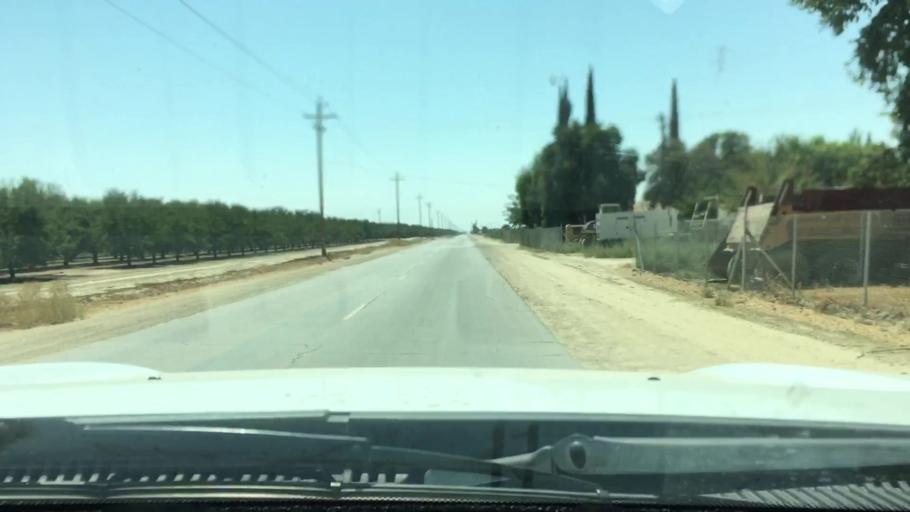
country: US
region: California
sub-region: Kern County
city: Wasco
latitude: 35.6627
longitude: -119.4375
